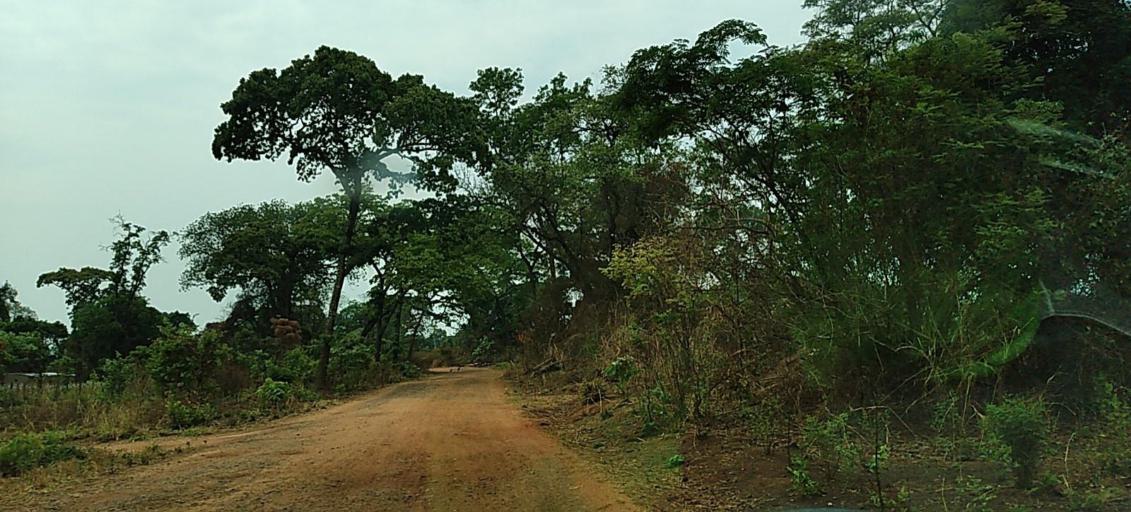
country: ZM
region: North-Western
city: Solwezi
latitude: -12.3413
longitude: 26.5261
